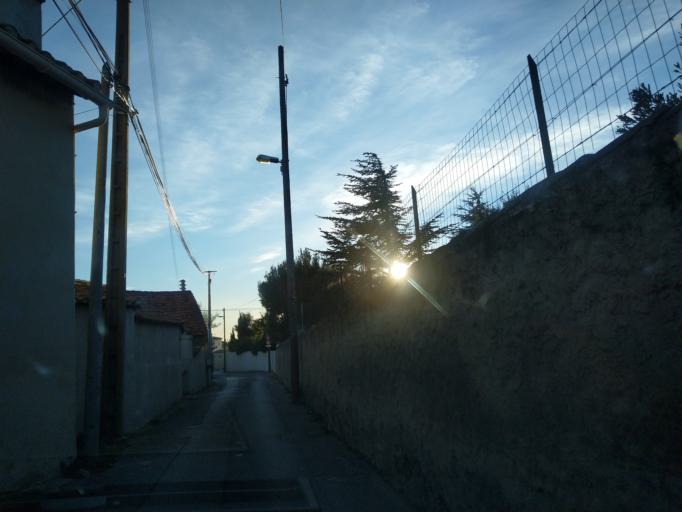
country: FR
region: Provence-Alpes-Cote d'Azur
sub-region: Departement des Bouches-du-Rhone
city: Plan-de-Cuques
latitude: 43.3522
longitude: 5.4571
